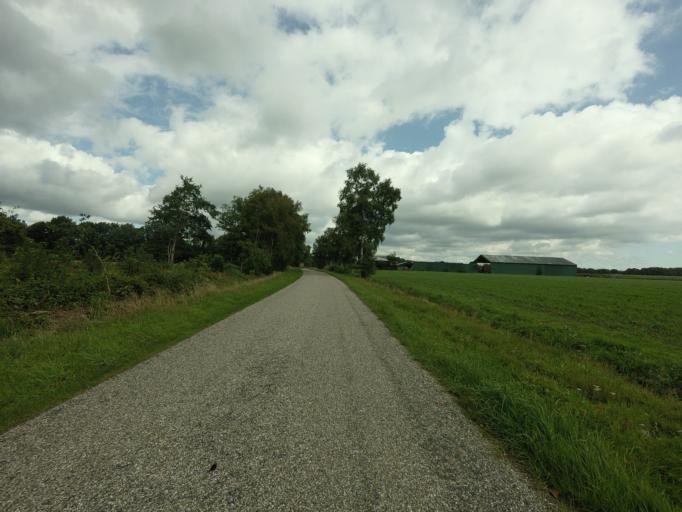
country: NL
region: Friesland
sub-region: Gemeente Heerenveen
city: Jubbega
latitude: 52.9781
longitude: 6.2773
